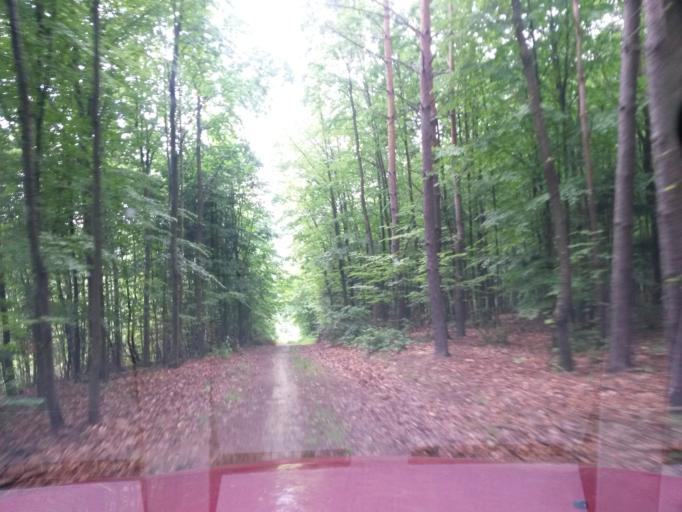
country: SK
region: Kosicky
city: Kosice
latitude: 48.7219
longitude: 21.1484
